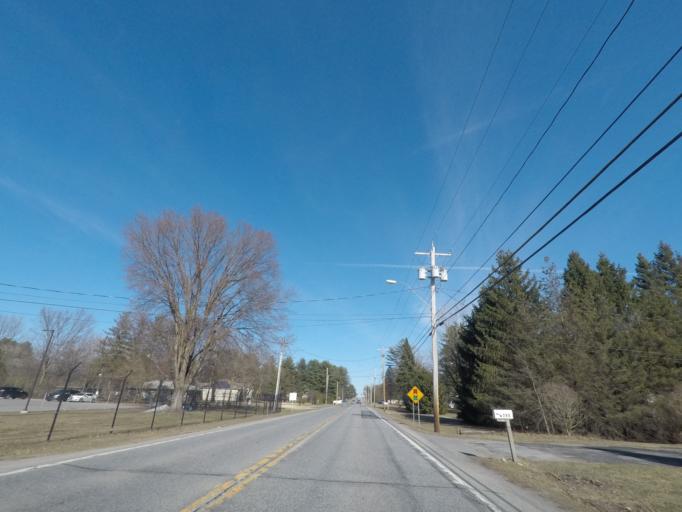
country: US
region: New York
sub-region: Saratoga County
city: Saratoga Springs
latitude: 43.0779
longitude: -73.8199
